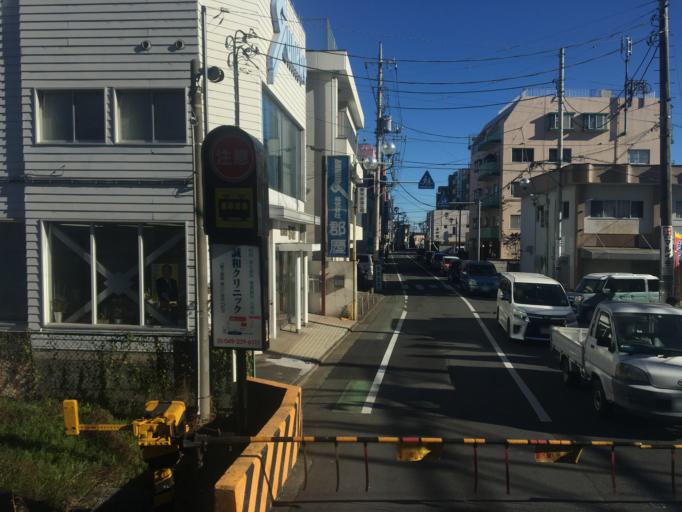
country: JP
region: Saitama
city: Sakado
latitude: 35.9376
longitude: 139.4228
